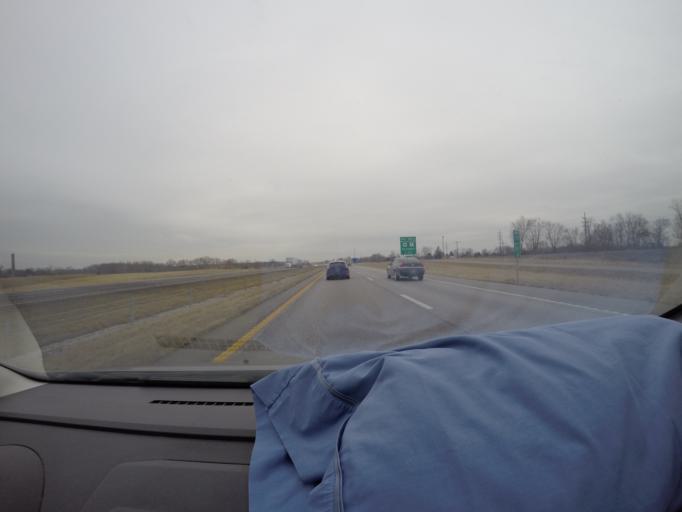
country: US
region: Missouri
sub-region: Warren County
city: Wright City
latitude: 38.8198
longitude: -90.9739
